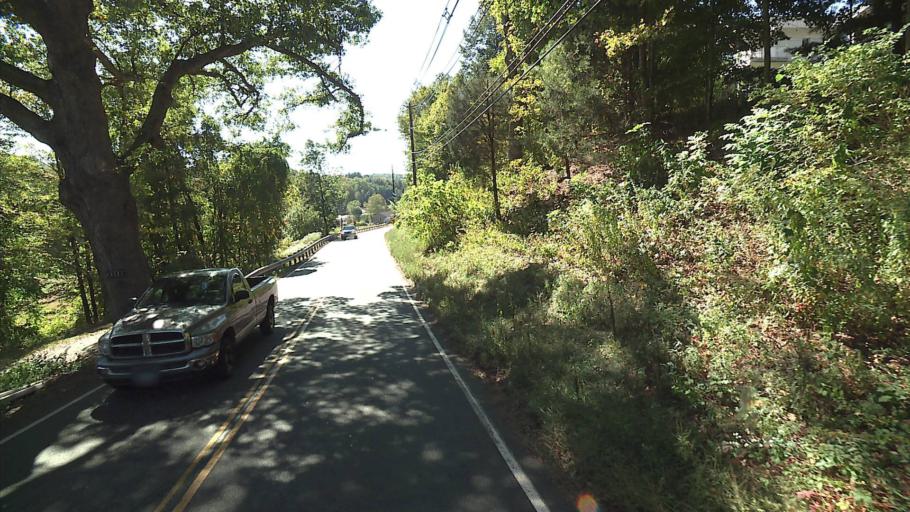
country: US
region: Connecticut
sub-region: Hartford County
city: Glastonbury Center
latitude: 41.6933
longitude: -72.5343
